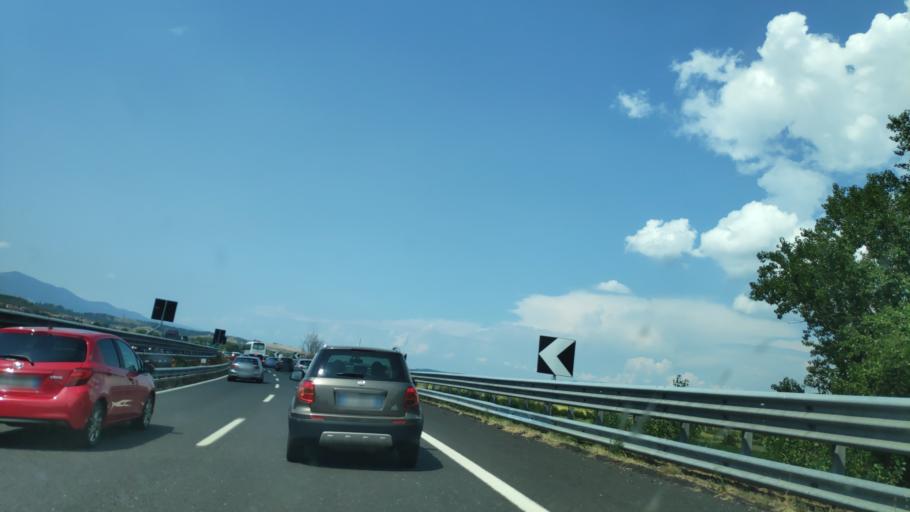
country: IT
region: Umbria
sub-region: Provincia di Terni
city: Fabro Scalo
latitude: 42.8612
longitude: 12.0374
